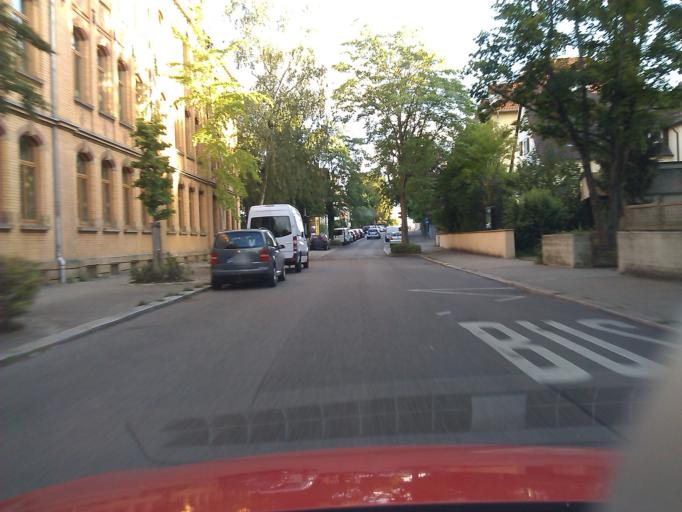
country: DE
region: Baden-Wuerttemberg
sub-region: Regierungsbezirk Stuttgart
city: Heilbronn
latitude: 49.1345
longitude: 9.1905
